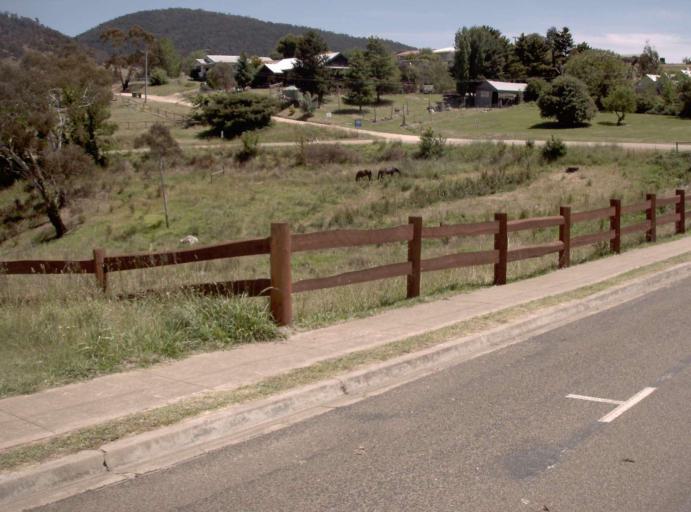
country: AU
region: Victoria
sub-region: Alpine
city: Mount Beauty
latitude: -37.0977
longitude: 147.5947
